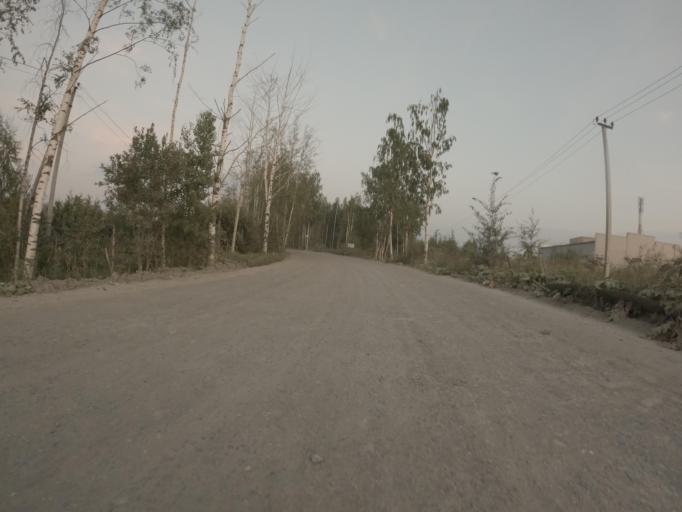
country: RU
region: Leningrad
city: Yanino Vtoroye
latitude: 59.9429
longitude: 30.5980
